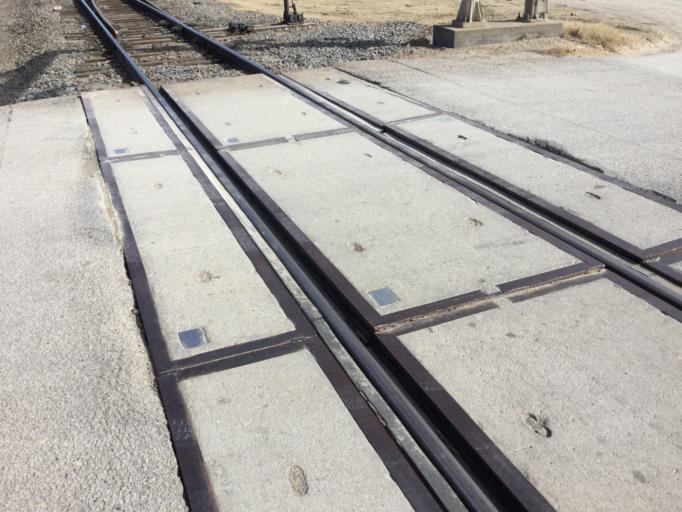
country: US
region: Kansas
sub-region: Saline County
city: Salina
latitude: 38.8790
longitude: -97.5110
